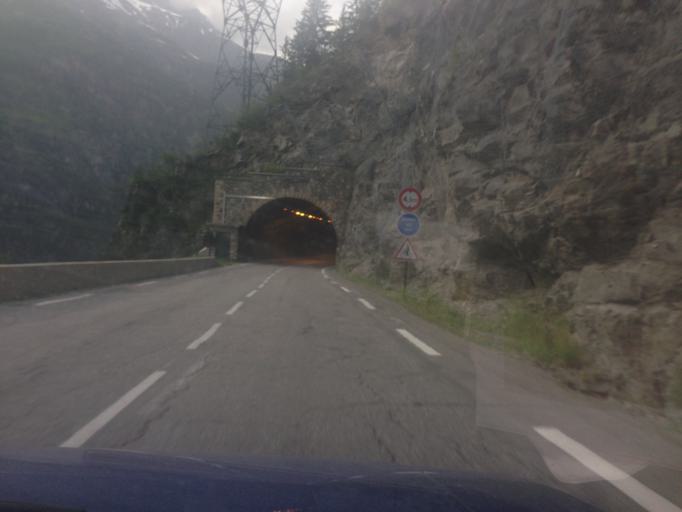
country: FR
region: Rhone-Alpes
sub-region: Departement de la Savoie
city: Tignes
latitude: 45.5048
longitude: 6.9288
